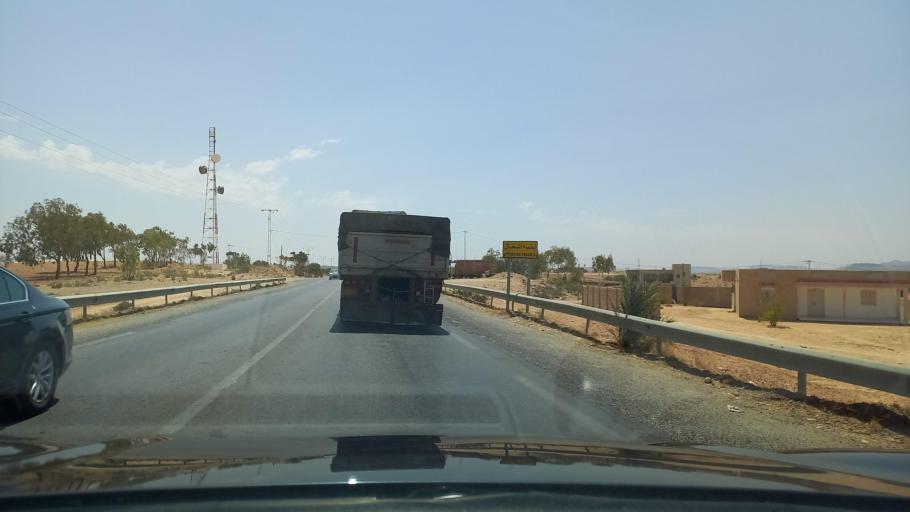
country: TN
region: Madanin
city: Medenine
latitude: 33.5706
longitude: 10.3171
